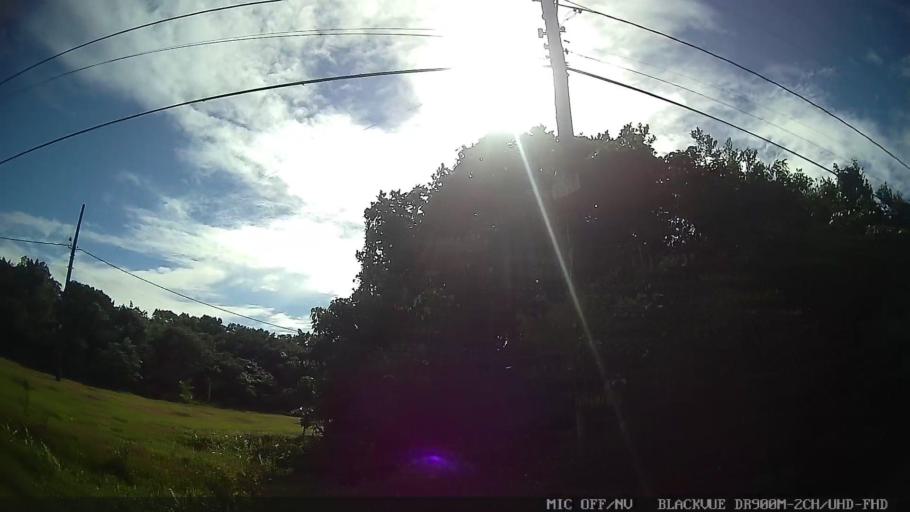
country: BR
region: Sao Paulo
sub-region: Peruibe
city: Peruibe
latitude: -24.2481
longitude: -46.9042
